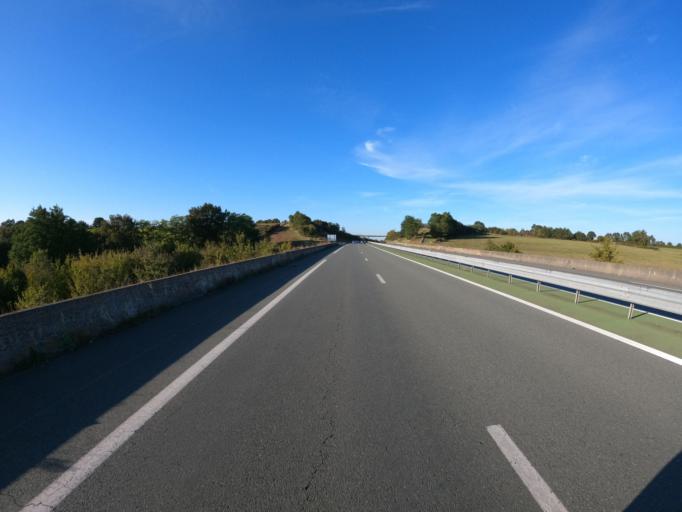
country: FR
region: Pays de la Loire
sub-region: Departement de Maine-et-Loire
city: Nuaille
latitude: 47.1051
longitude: -0.8269
